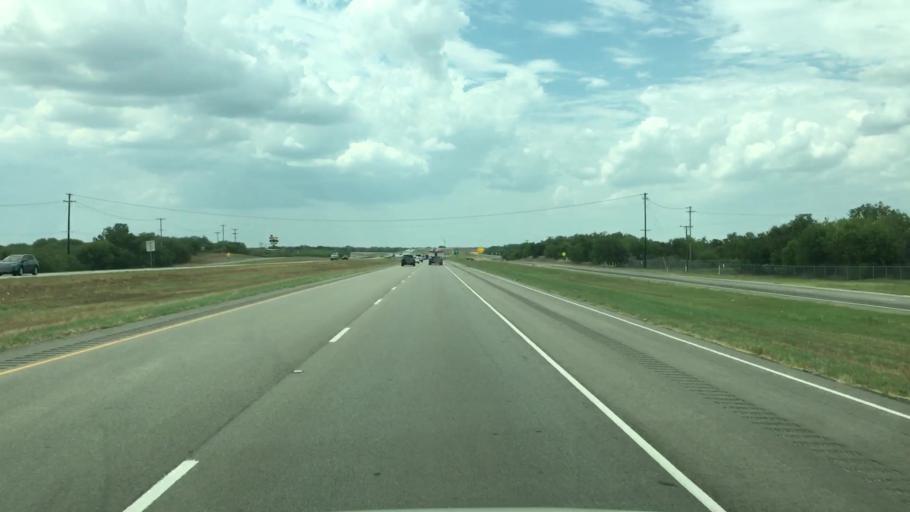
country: US
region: Texas
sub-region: Live Oak County
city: Three Rivers
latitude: 28.5155
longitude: -98.1744
